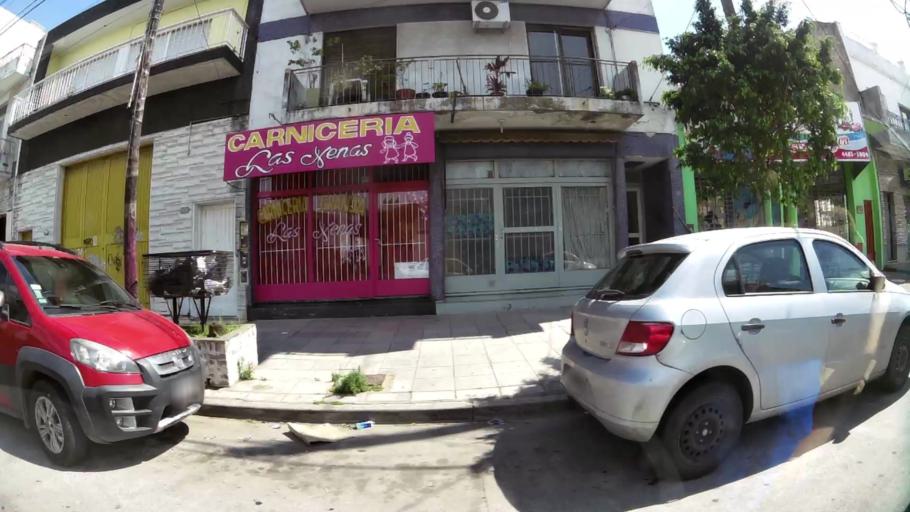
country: AR
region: Buenos Aires
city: San Justo
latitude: -34.6744
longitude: -58.5663
